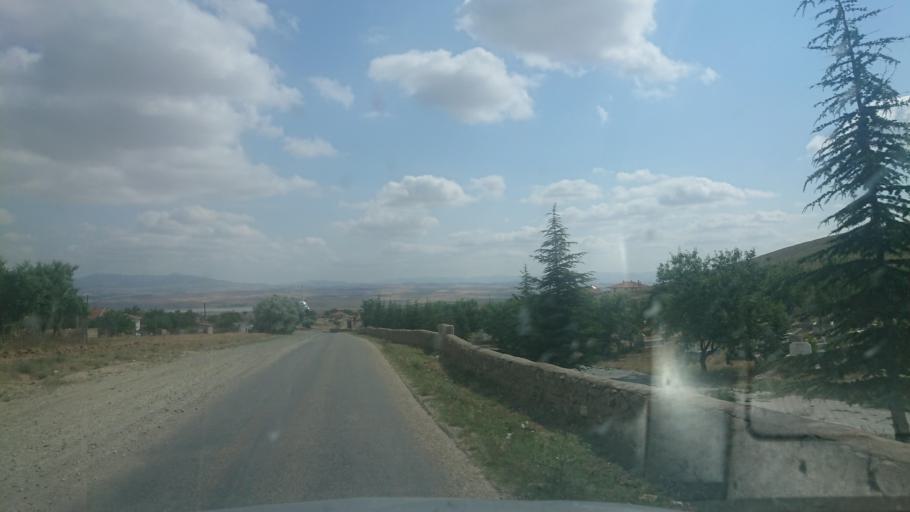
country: TR
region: Aksaray
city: Sariyahsi
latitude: 39.0097
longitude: 33.9431
